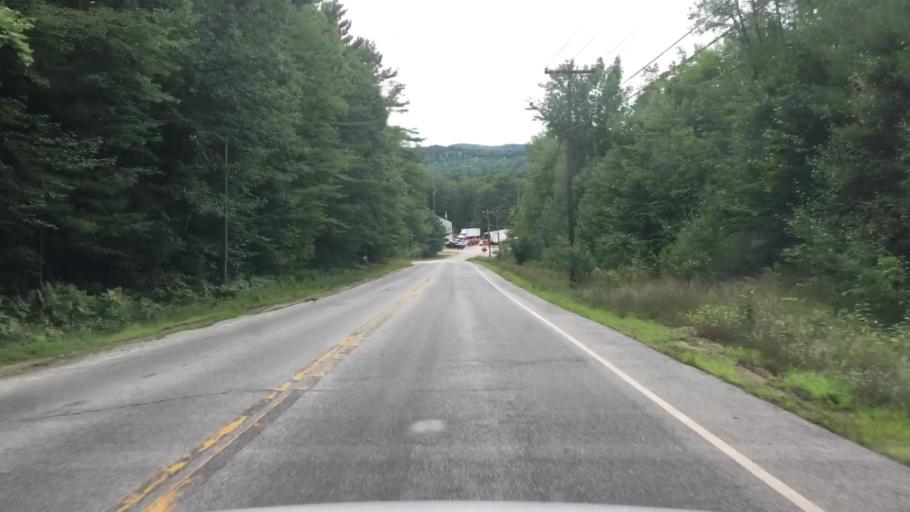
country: US
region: Maine
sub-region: York County
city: Cornish
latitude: 43.8103
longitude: -70.7780
